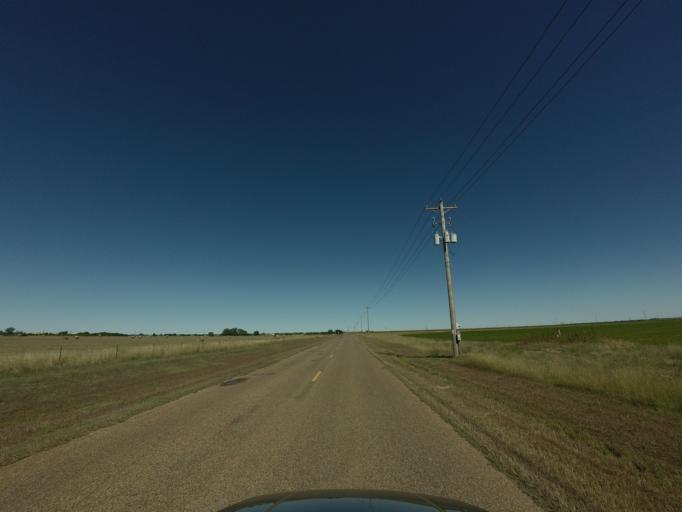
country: US
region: New Mexico
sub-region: Curry County
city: Clovis
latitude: 34.4299
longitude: -103.1608
